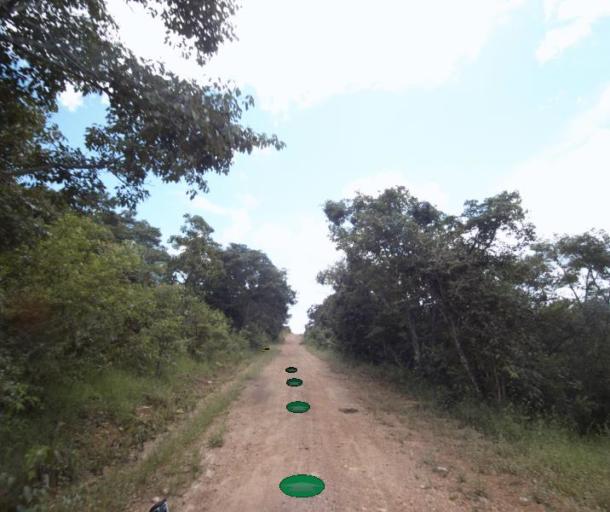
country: BR
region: Goias
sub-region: Pirenopolis
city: Pirenopolis
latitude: -15.7878
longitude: -48.9183
